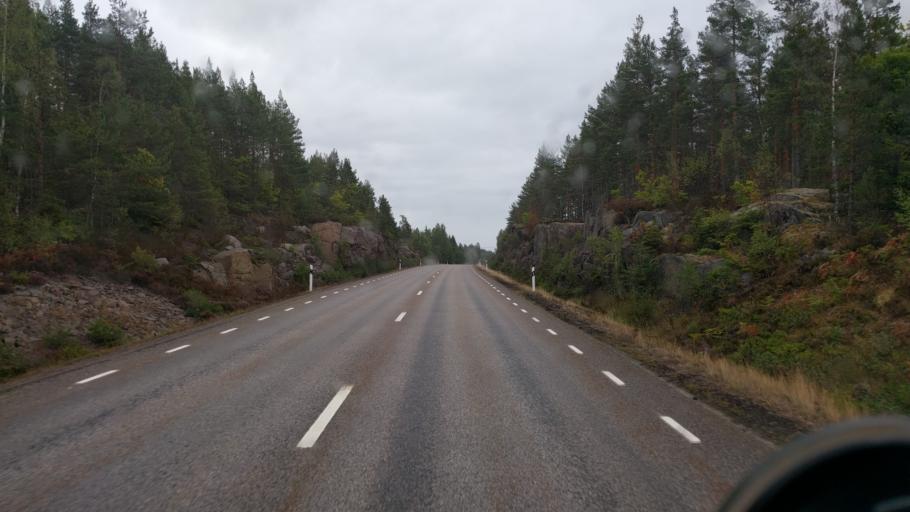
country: SE
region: Kalmar
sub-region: Vasterviks Kommun
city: Ankarsrum
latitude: 57.7009
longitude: 16.2421
